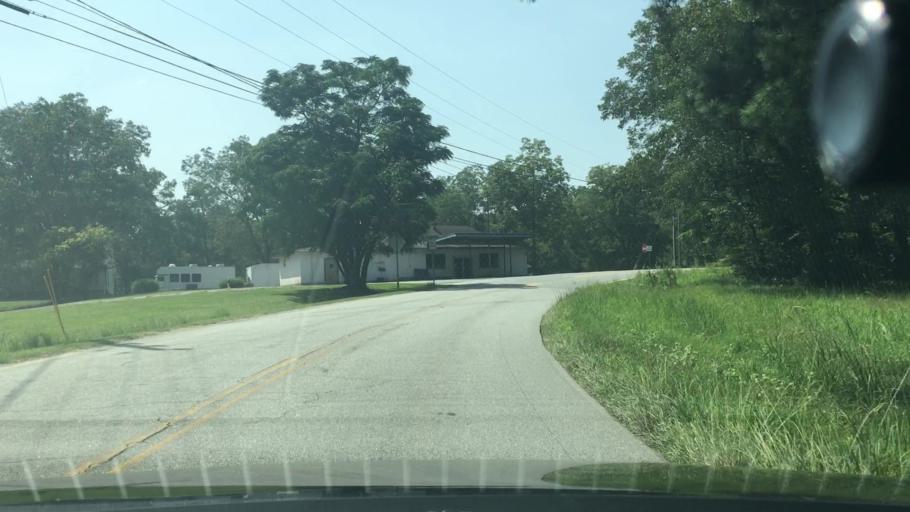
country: US
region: Georgia
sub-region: Coweta County
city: East Newnan
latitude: 33.3539
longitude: -84.7702
